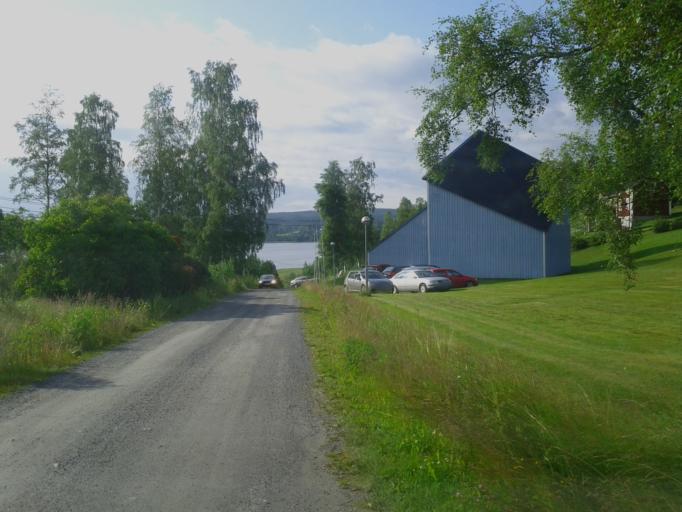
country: SE
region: Vaesternorrland
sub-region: OErnskoeldsviks Kommun
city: Ornskoldsvik
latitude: 63.2567
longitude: 18.8109
